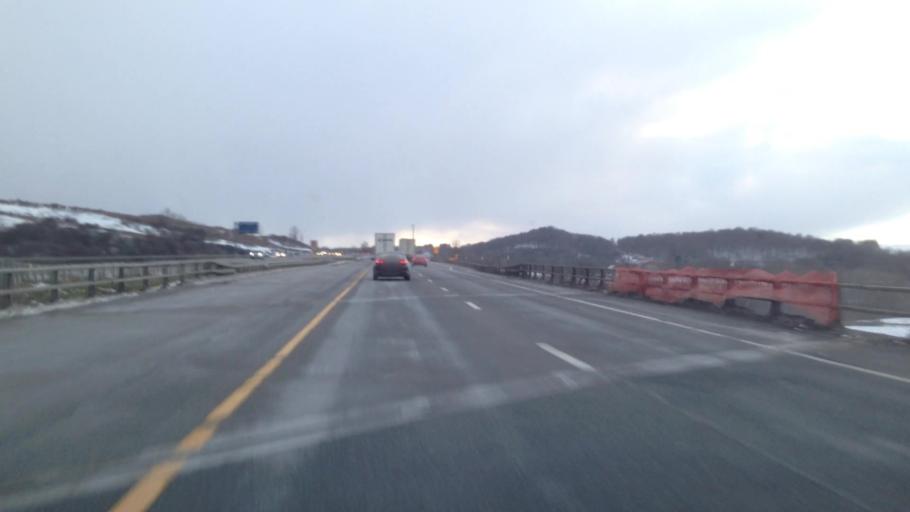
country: US
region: New York
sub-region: Herkimer County
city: Little Falls
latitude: 43.0172
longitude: -74.8109
